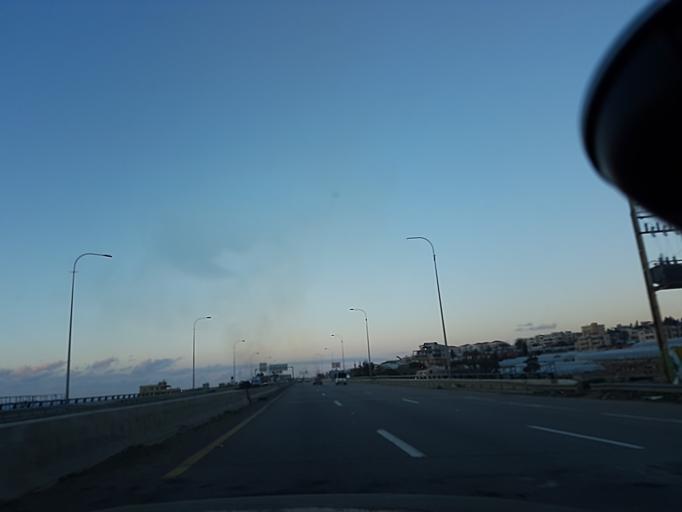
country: LB
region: Liban-Sud
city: Sidon
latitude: 33.6246
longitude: 35.4021
